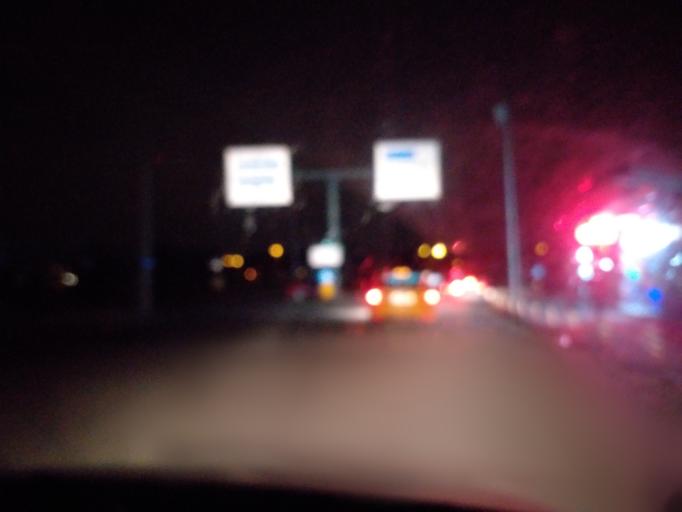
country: TR
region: Ankara
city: Batikent
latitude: 39.9050
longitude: 32.7329
